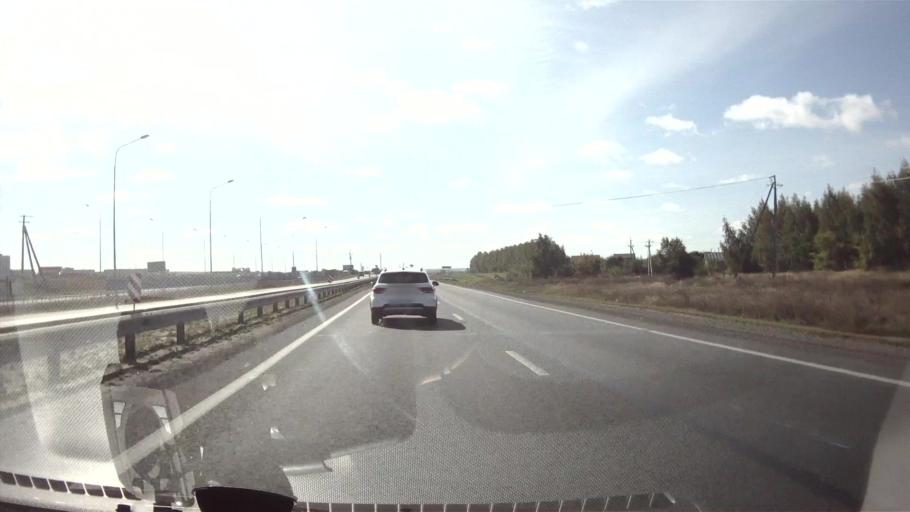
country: RU
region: Ulyanovsk
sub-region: Ulyanovskiy Rayon
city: Ulyanovsk
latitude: 54.2818
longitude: 48.2583
